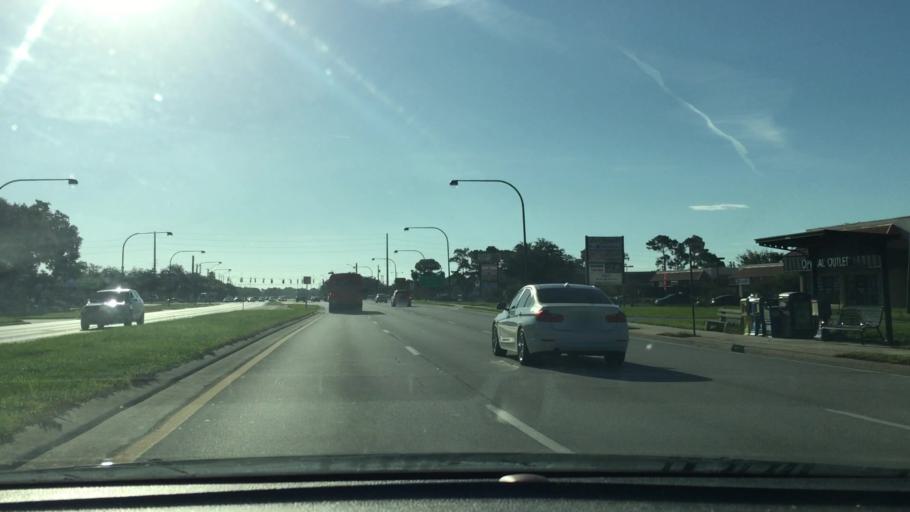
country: US
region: Florida
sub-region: Osceola County
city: Kissimmee
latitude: 28.3044
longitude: -81.3942
